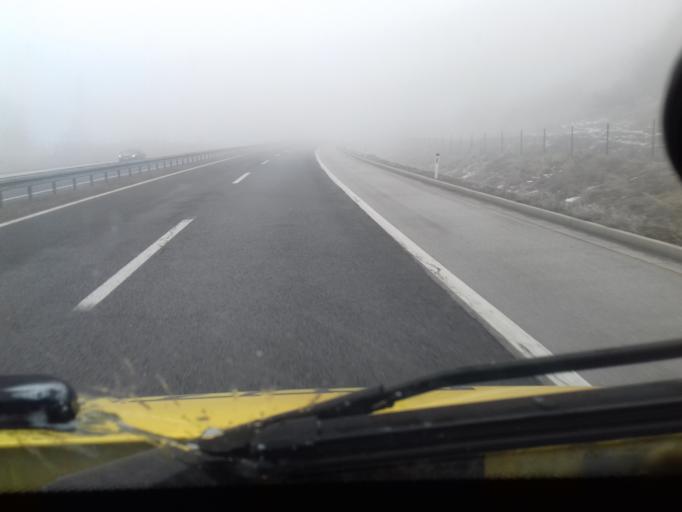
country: BA
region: Federation of Bosnia and Herzegovina
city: Visoko
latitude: 43.9926
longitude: 18.2172
